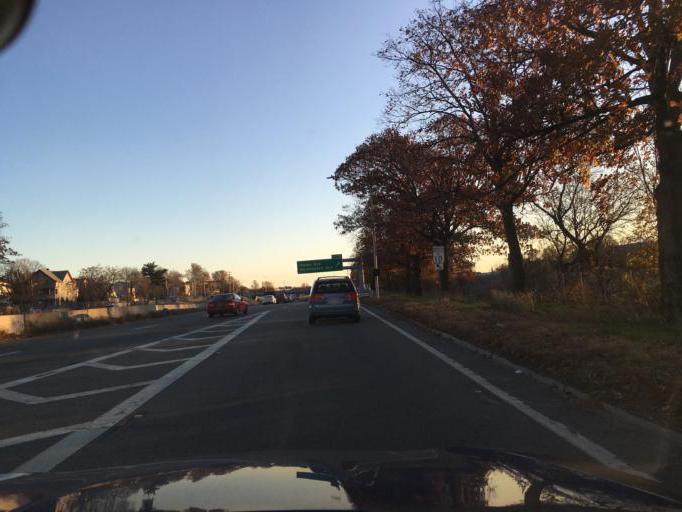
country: US
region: Rhode Island
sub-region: Providence County
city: Providence
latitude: 41.8120
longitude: -71.4405
